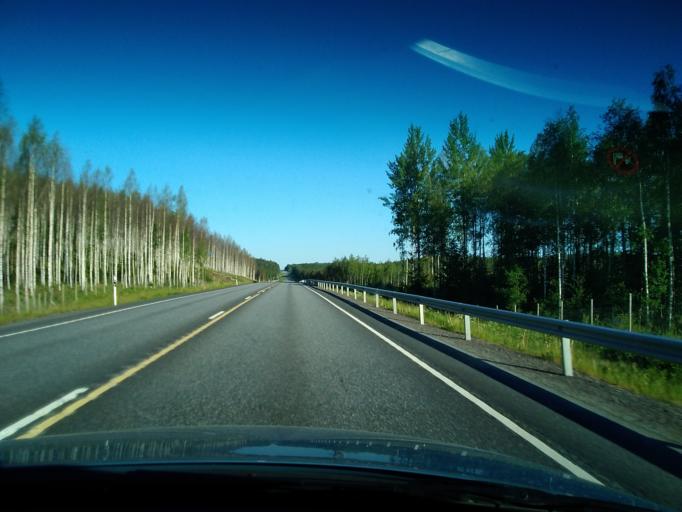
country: FI
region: Uusimaa
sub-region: Helsinki
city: Kaerkoelae
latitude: 60.6204
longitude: 24.0016
